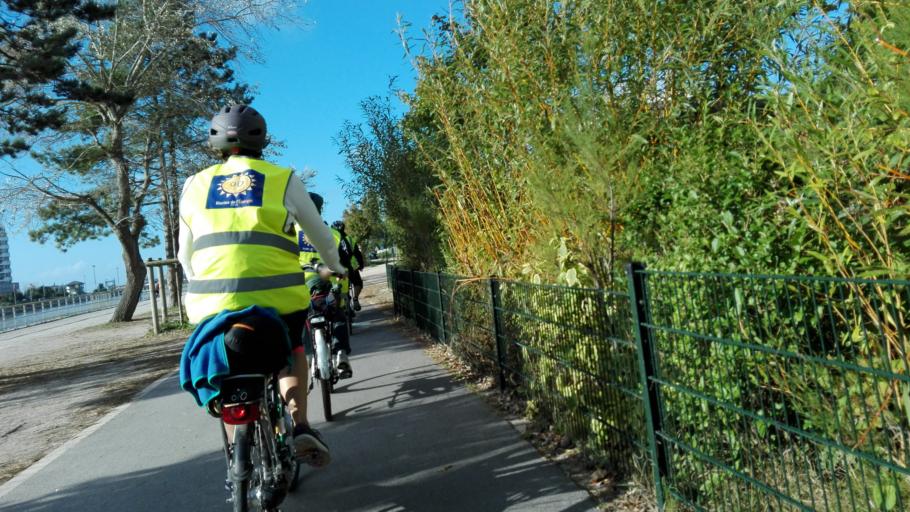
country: FR
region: Nord-Pas-de-Calais
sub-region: Departement du Pas-de-Calais
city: Boulogne-sur-Mer
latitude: 50.7163
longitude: 1.6061
